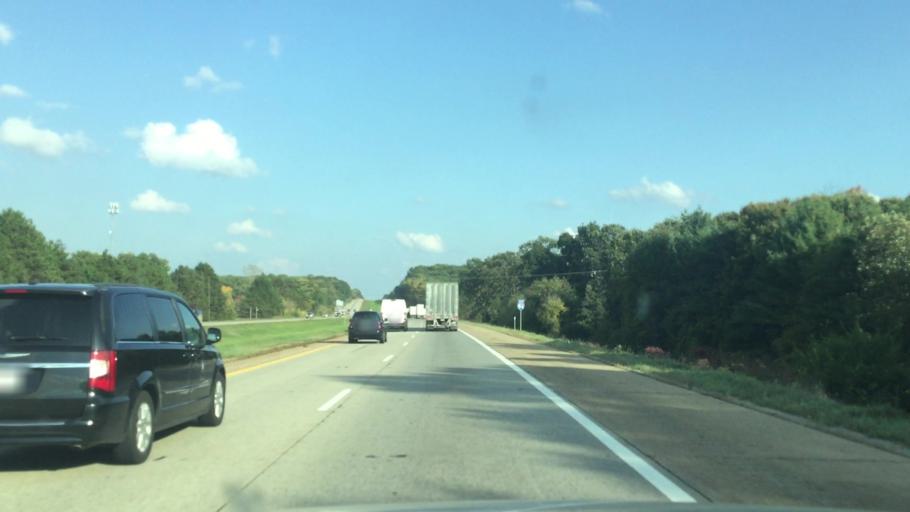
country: US
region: Michigan
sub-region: Calhoun County
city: Albion
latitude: 42.2619
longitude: -84.6989
